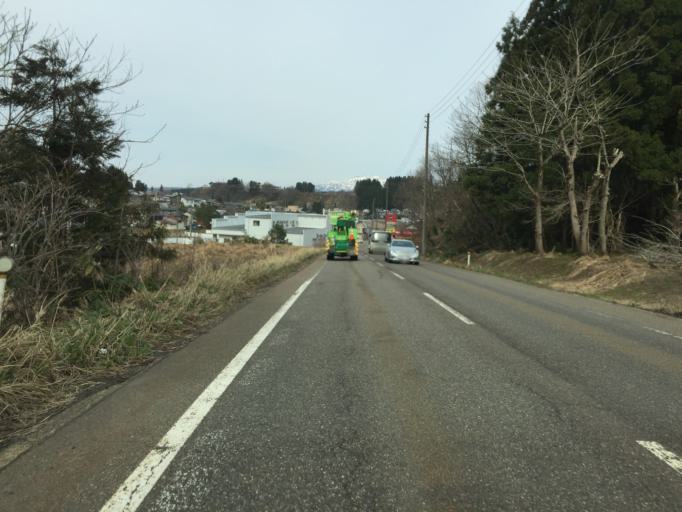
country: JP
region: Niigata
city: Tochio-honcho
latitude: 37.4649
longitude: 138.9864
